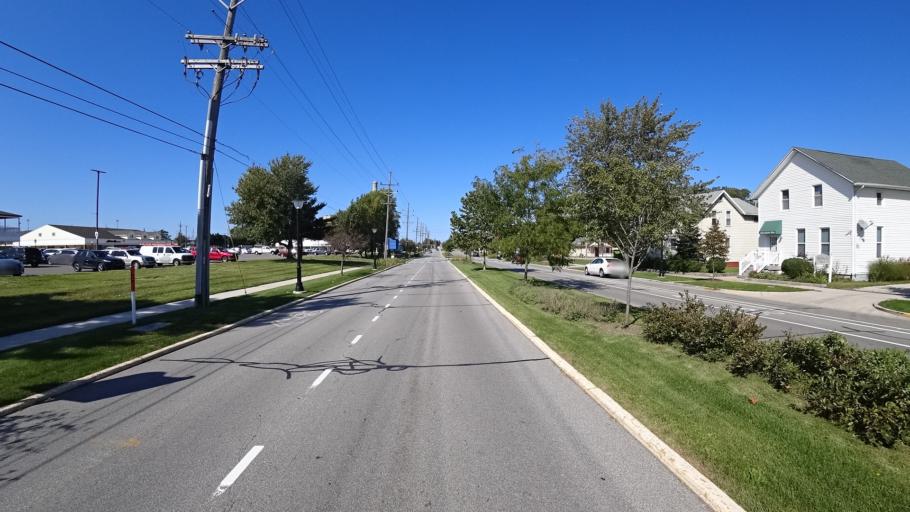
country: US
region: Indiana
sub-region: LaPorte County
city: Michigan City
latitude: 41.7157
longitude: -86.9045
